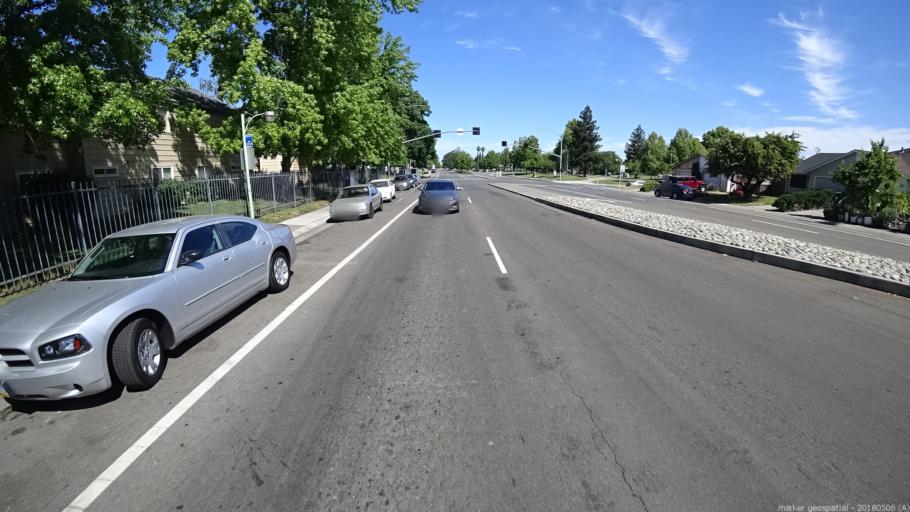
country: US
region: California
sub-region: Sacramento County
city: Laguna
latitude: 38.4595
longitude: -121.4291
